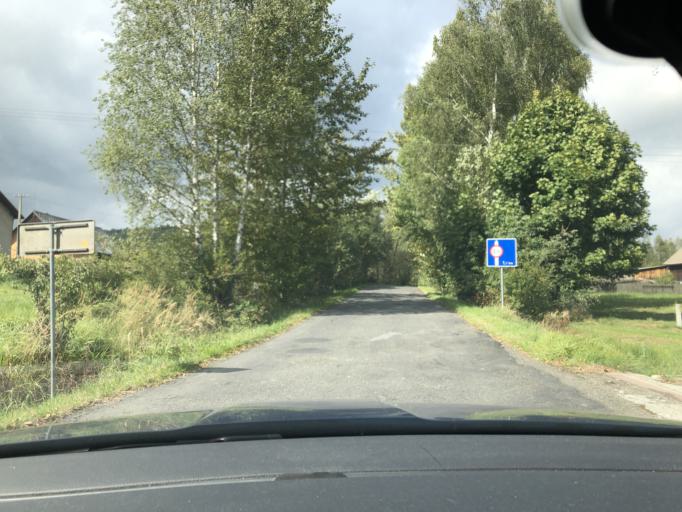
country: PL
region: Lesser Poland Voivodeship
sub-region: Powiat suski
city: Lachowice
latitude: 49.7074
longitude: 19.4218
